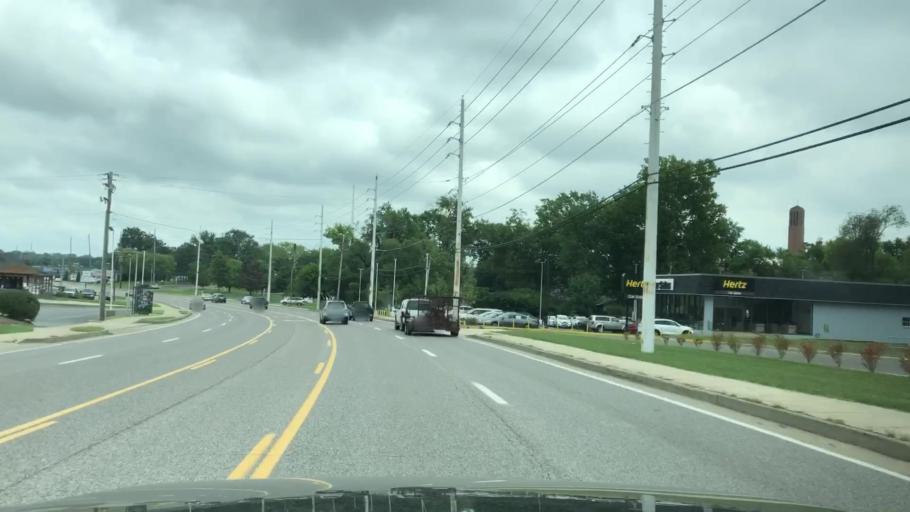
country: US
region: Missouri
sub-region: Saint Louis County
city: Florissant
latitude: 38.7980
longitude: -90.3210
